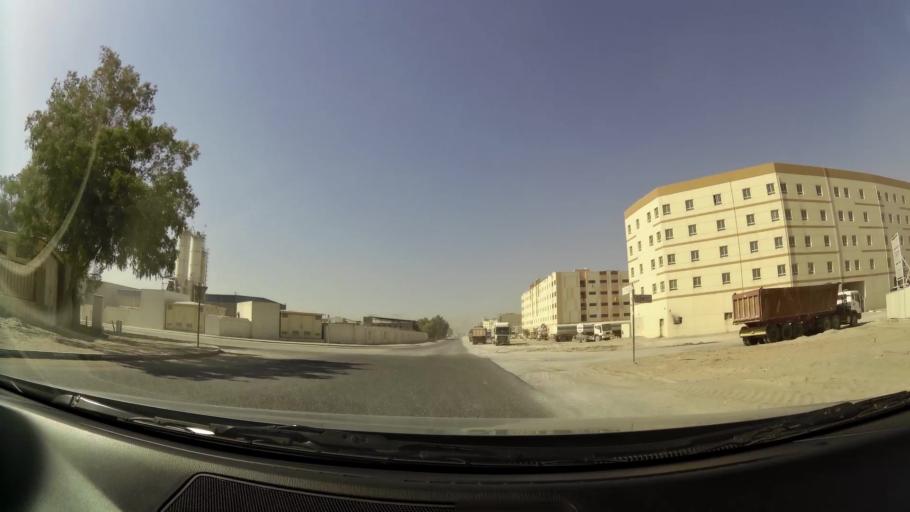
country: AE
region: Dubai
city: Dubai
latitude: 24.9928
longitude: 55.1398
